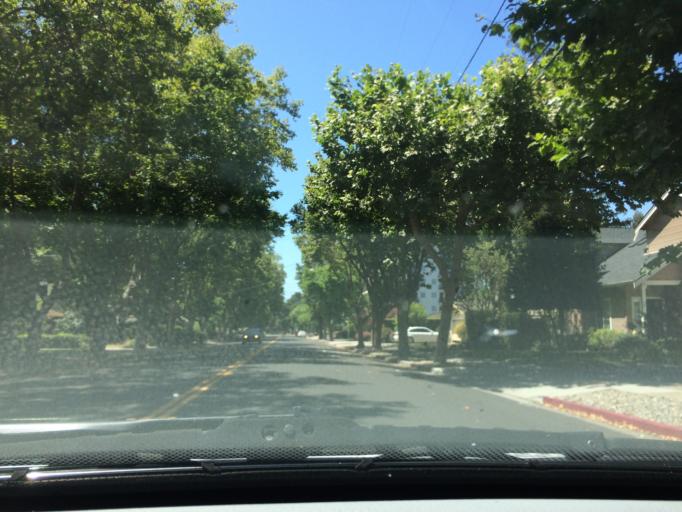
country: US
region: California
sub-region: San Mateo County
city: Menlo Park
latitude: 37.4511
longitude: -122.1884
